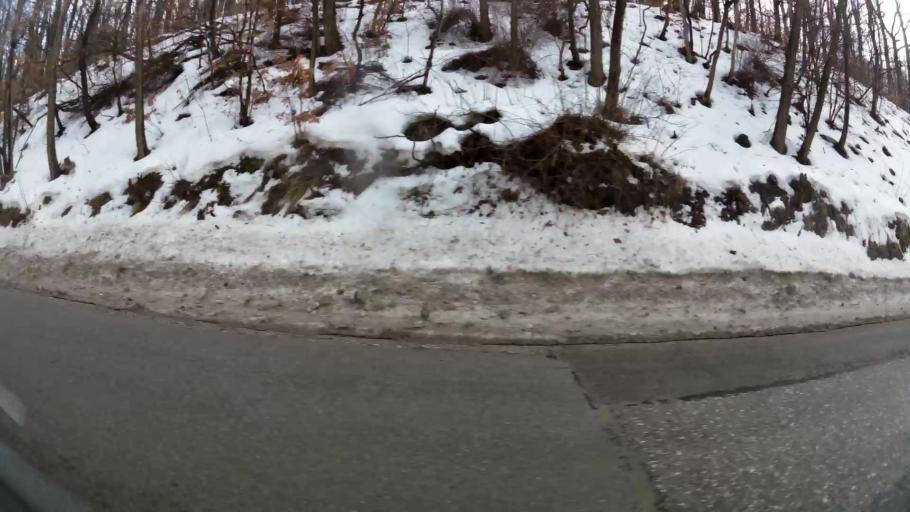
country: BG
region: Sofiya
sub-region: Obshtina Bozhurishte
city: Bozhurishte
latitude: 42.6361
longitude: 23.2220
